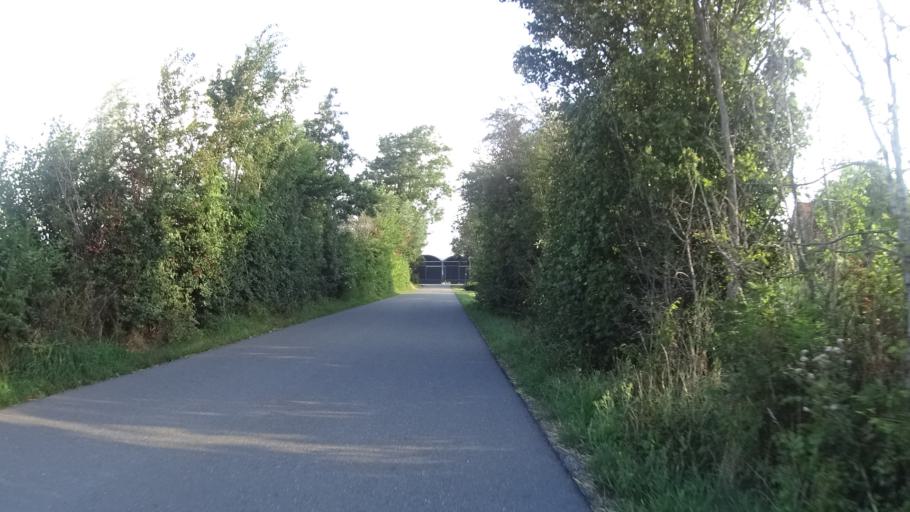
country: NL
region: Zeeland
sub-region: Gemeente Middelburg
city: Middelburg
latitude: 51.5219
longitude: 3.6264
